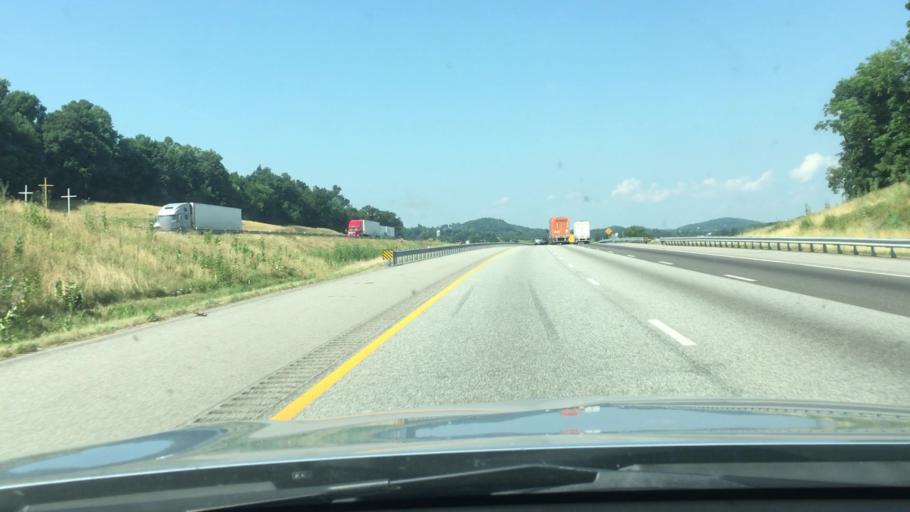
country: US
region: Virginia
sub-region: City of Buena Vista
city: Buena Vista
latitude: 37.8982
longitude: -79.2714
